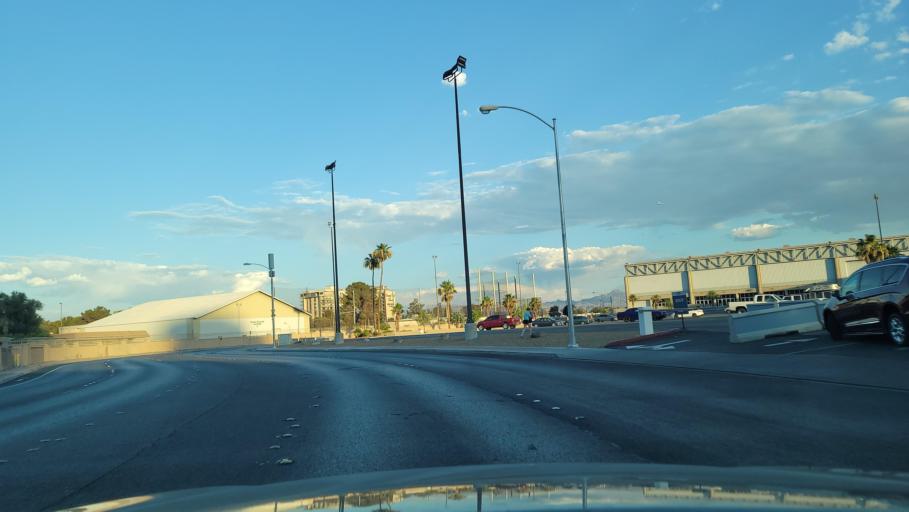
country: US
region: Nevada
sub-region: Clark County
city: Winchester
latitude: 36.1338
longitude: -115.1489
